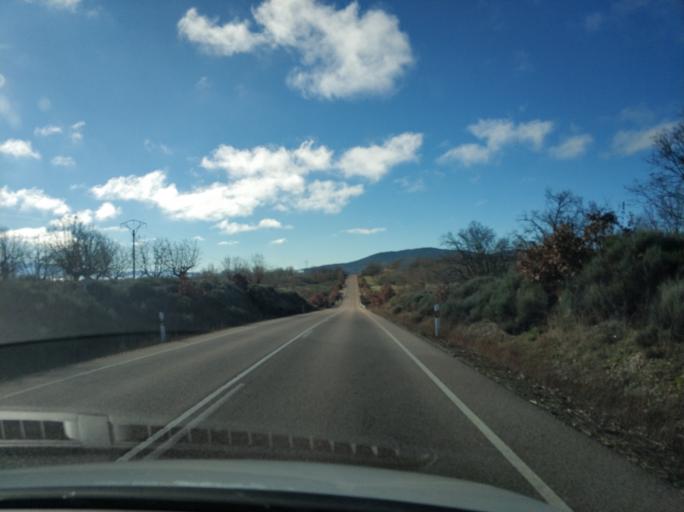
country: ES
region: Castille and Leon
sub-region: Provincia de Salamanca
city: Linares de Riofrio
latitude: 40.6153
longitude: -5.9092
